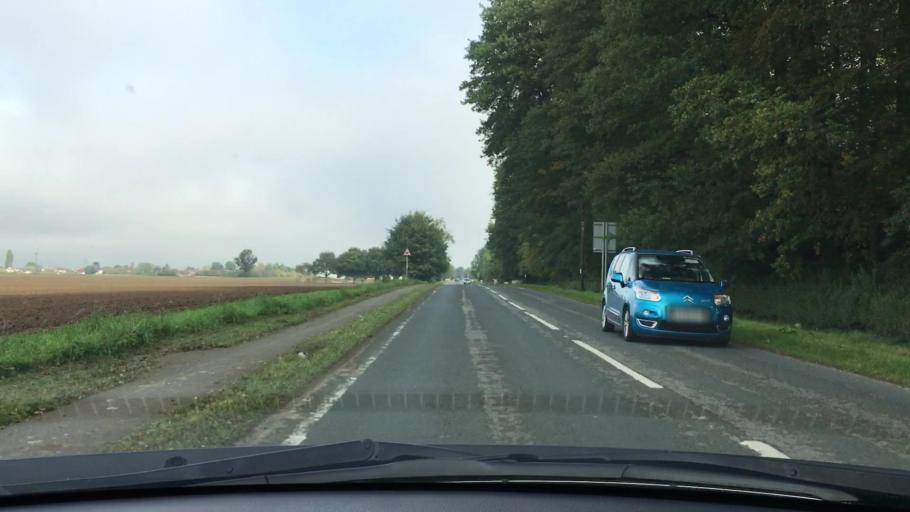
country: GB
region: England
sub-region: North East Lincolnshire
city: Waltham
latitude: 53.5120
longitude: -0.1295
